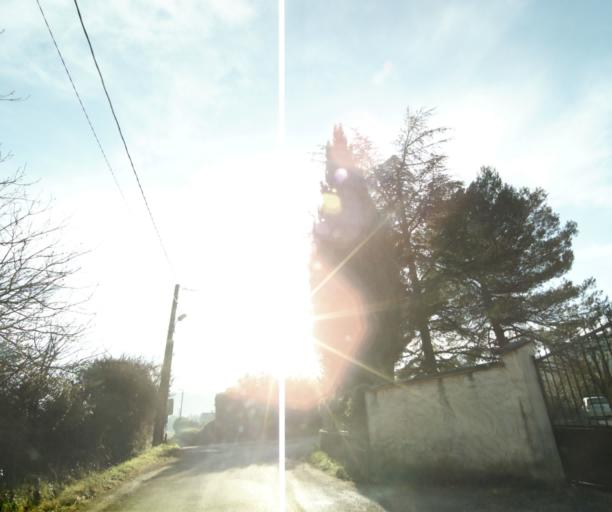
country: FR
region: Provence-Alpes-Cote d'Azur
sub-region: Departement du Var
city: Tourves
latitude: 43.4043
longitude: 5.9267
